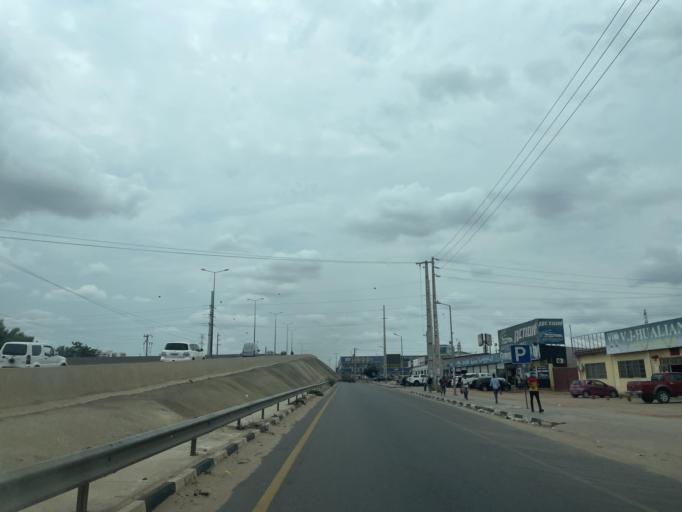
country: AO
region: Luanda
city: Luanda
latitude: -8.9771
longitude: 13.3929
